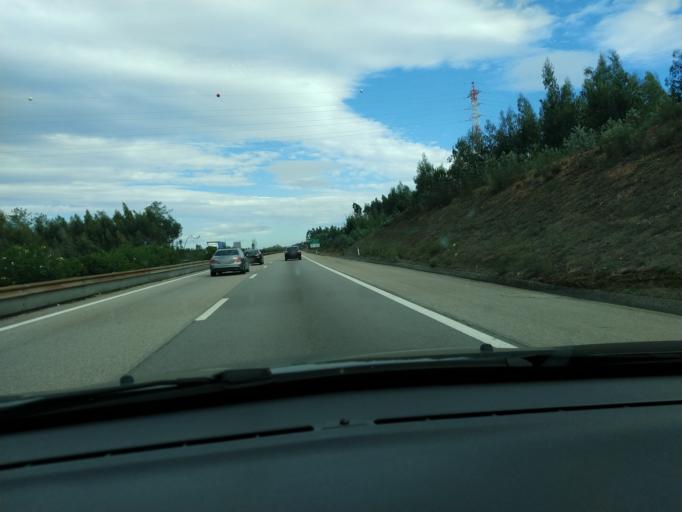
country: PT
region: Aveiro
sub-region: Albergaria-A-Velha
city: Albergaria-a-Velha
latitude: 40.7016
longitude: -8.5227
